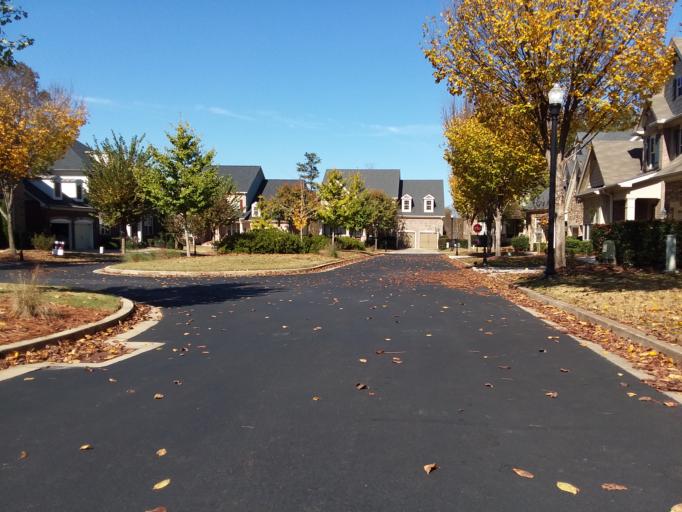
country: US
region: Georgia
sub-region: Fulton County
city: Johns Creek
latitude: 34.0253
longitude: -84.2560
